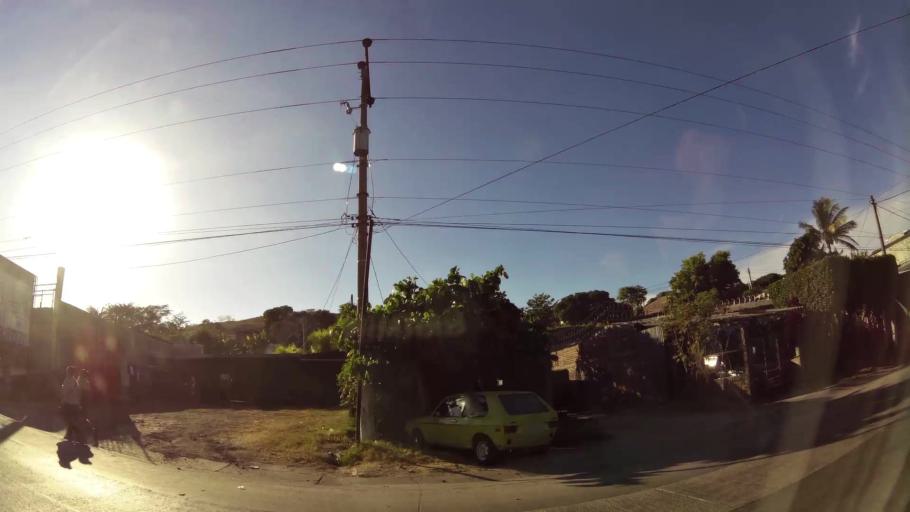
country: SV
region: Santa Ana
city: Metapan
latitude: 14.3211
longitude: -89.4446
